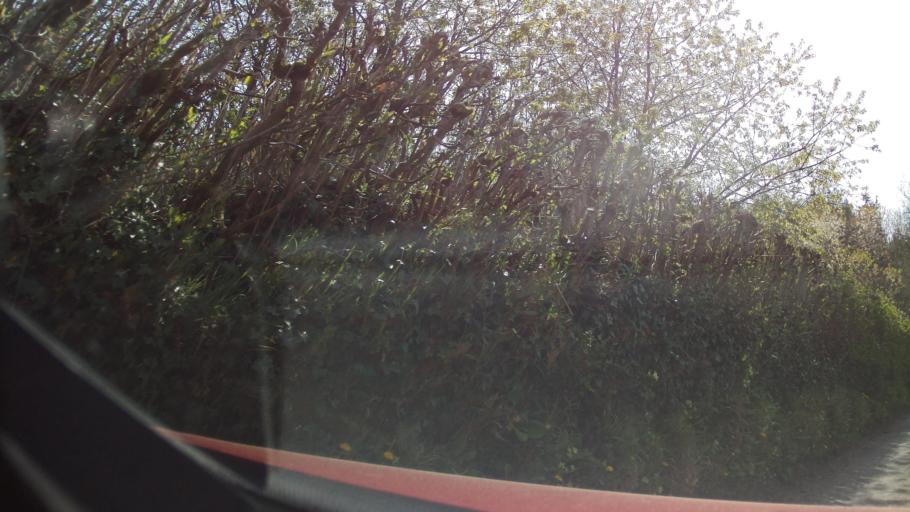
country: GB
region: England
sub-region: Dorset
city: Sherborne
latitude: 50.9742
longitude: -2.5327
